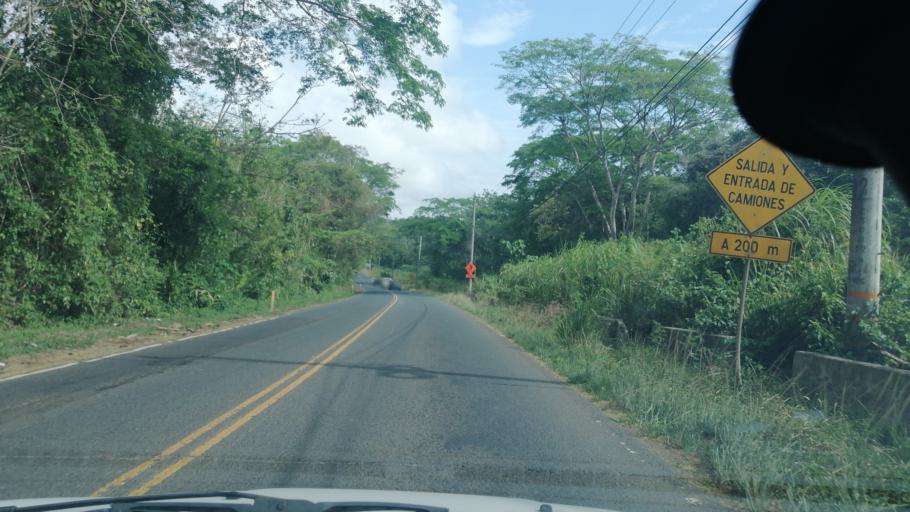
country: PA
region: Panama
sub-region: Distrito de Panama
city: Paraiso
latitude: 9.0438
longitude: -79.6351
